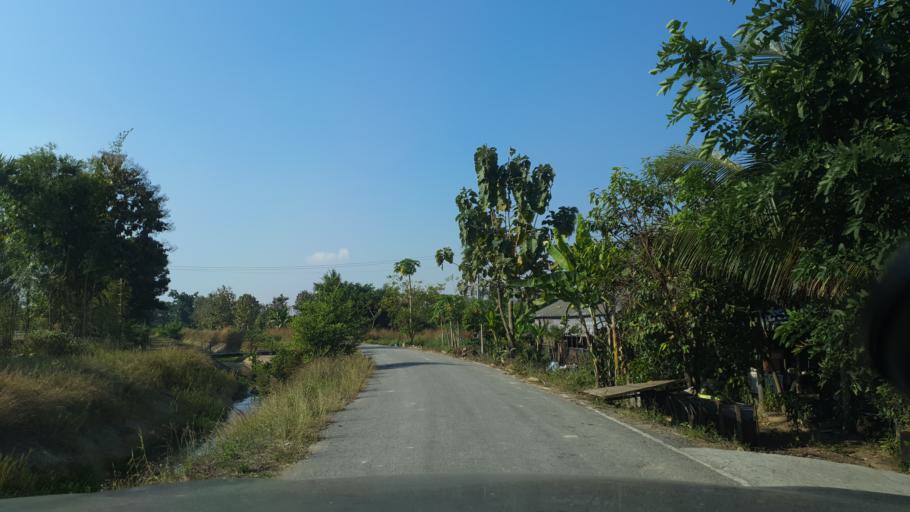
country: TH
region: Lamphun
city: Ban Thi
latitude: 18.6708
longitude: 99.1339
